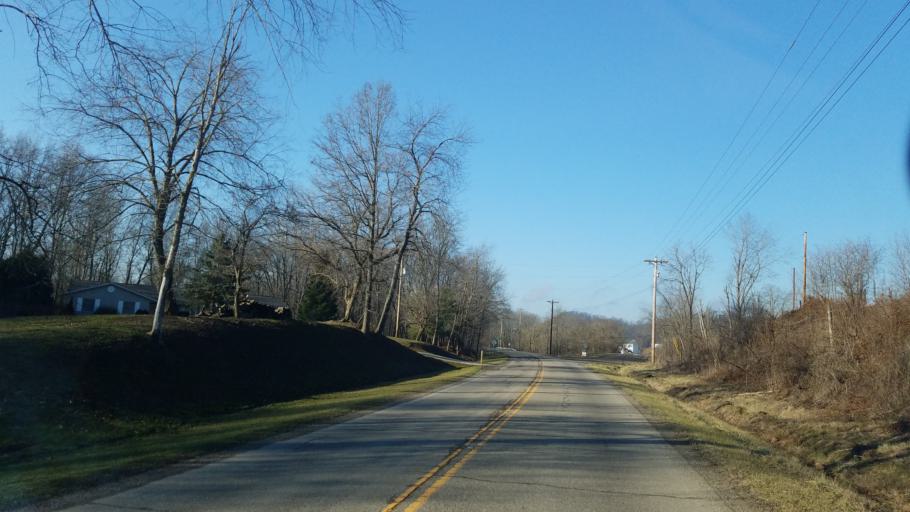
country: US
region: Ohio
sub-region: Guernsey County
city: Byesville
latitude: 40.0466
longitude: -81.3685
